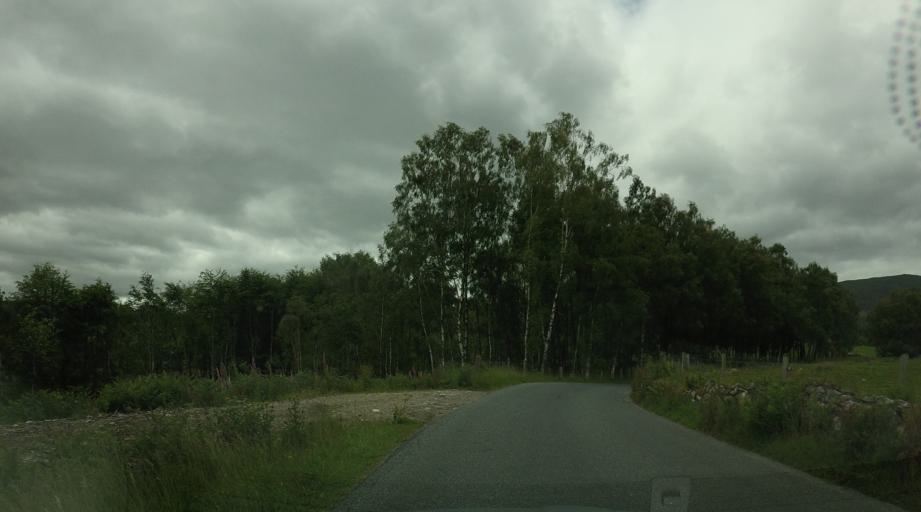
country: GB
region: Scotland
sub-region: Perth and Kinross
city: Aberfeldy
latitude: 56.7068
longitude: -4.0973
